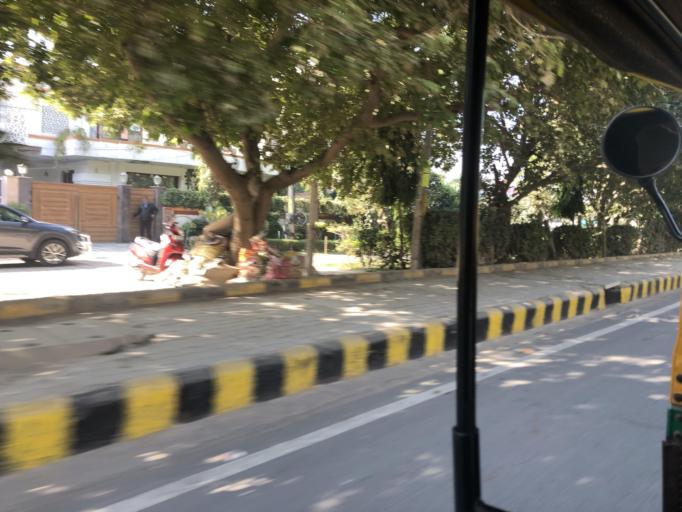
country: IN
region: Haryana
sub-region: Gurgaon
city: Gurgaon
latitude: 28.4517
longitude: 77.0673
